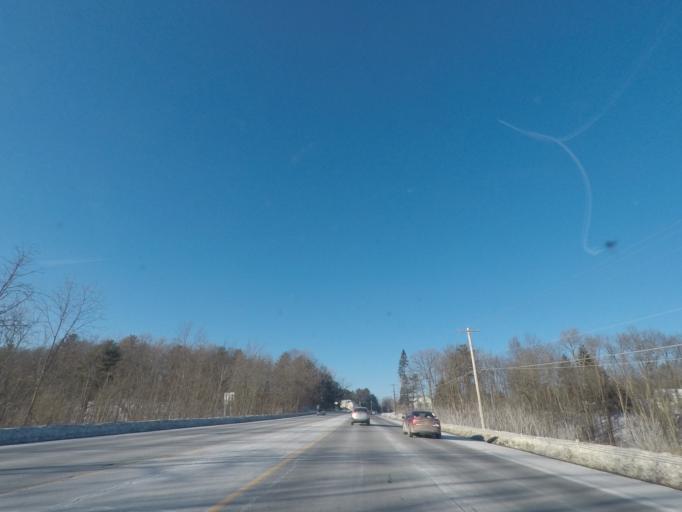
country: US
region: New York
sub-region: Saratoga County
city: Saratoga Springs
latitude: 43.0405
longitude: -73.7904
